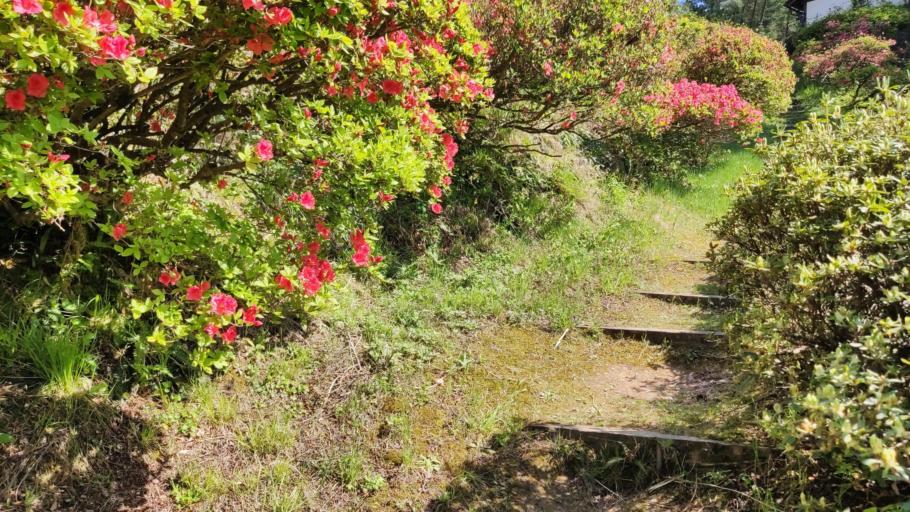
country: JP
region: Yamagata
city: Tendo
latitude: 38.3563
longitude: 140.3750
